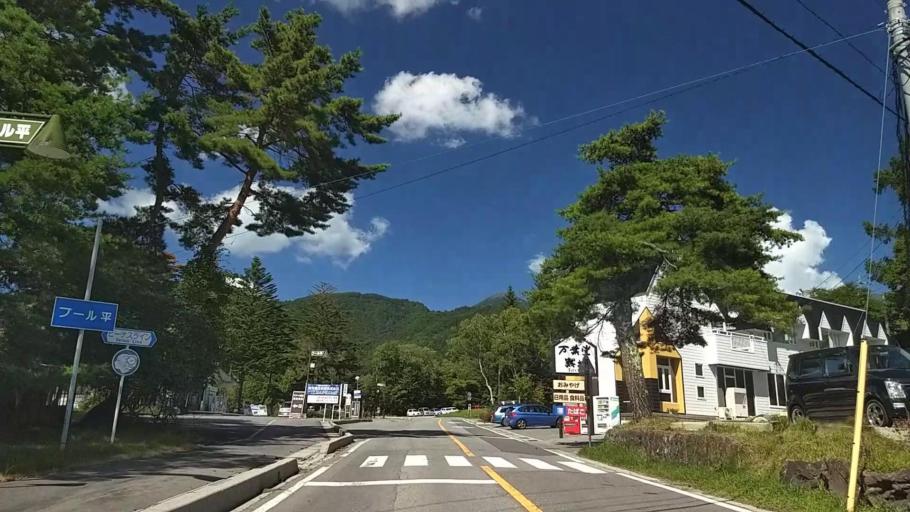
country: JP
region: Nagano
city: Chino
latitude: 36.0577
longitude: 138.2673
